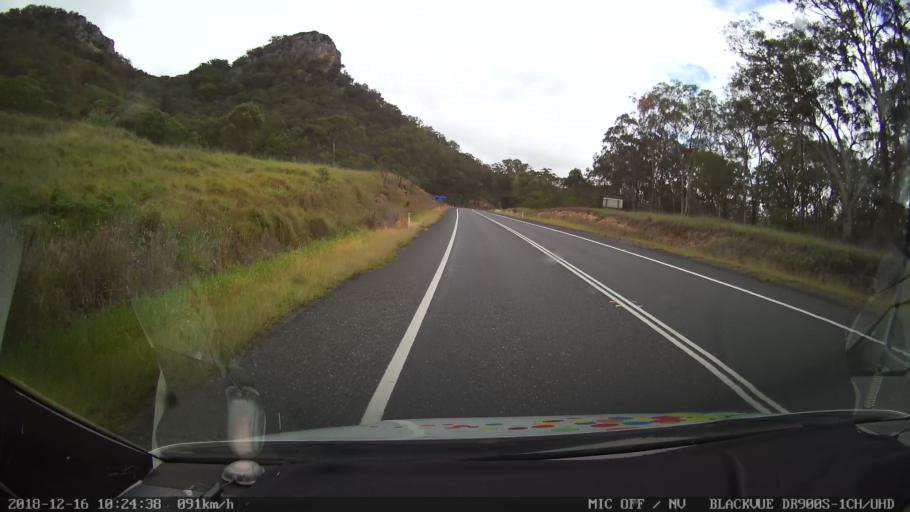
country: AU
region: New South Wales
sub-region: Tenterfield Municipality
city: Carrolls Creek
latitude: -29.1683
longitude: 152.0050
